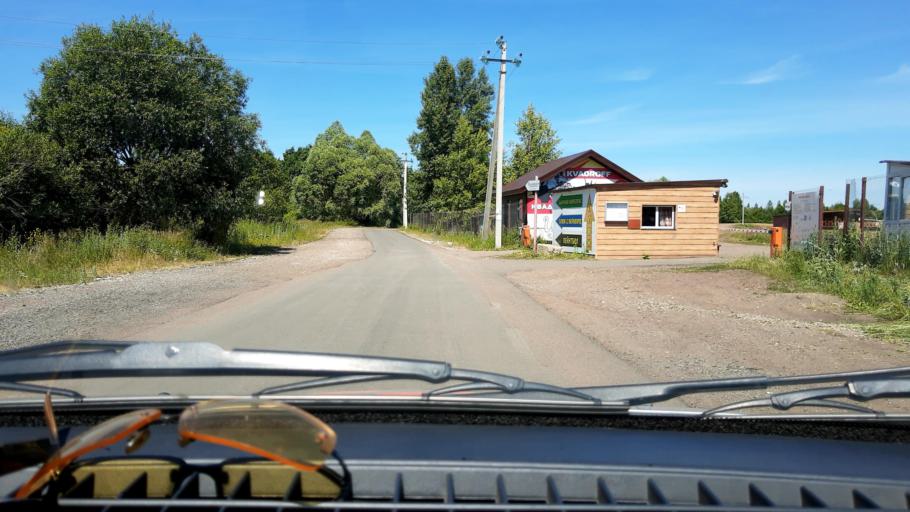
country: RU
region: Bashkortostan
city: Blagoveshchensk
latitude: 54.9675
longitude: 55.8137
